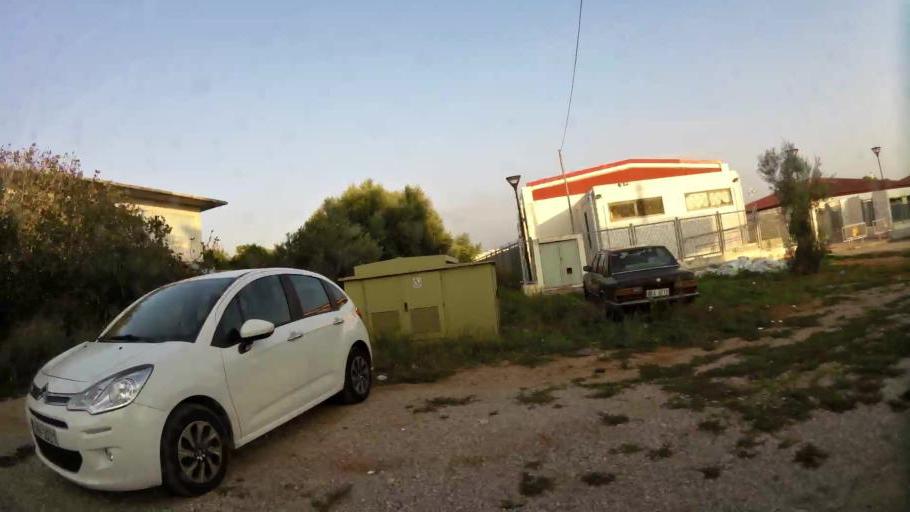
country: GR
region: Attica
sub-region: Nomarchia Anatolikis Attikis
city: Acharnes
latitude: 38.0961
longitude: 23.7444
